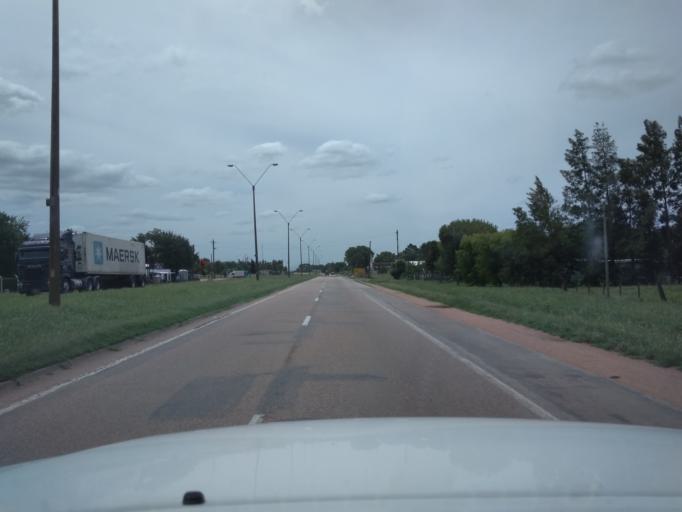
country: UY
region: Canelones
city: Joanico
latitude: -34.5972
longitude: -56.2619
